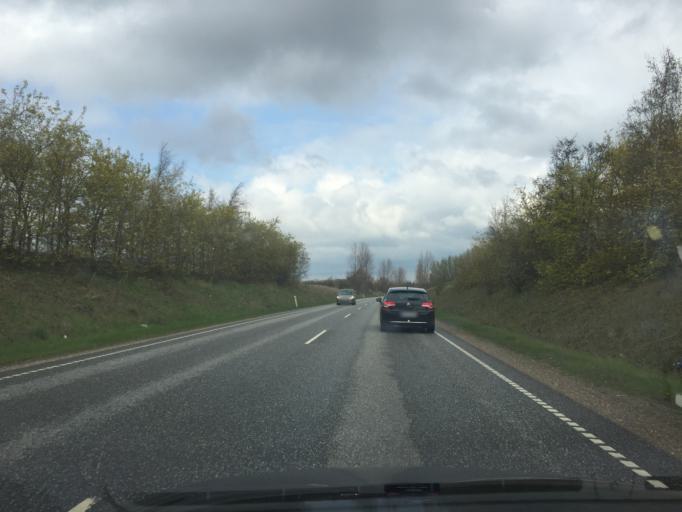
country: DK
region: Zealand
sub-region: Roskilde Kommune
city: Jyllinge
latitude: 55.7995
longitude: 12.1041
